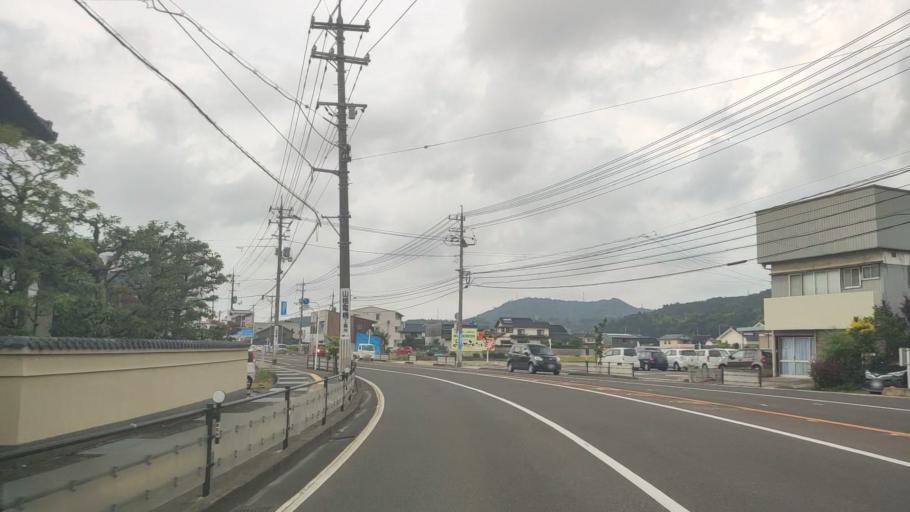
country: JP
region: Tottori
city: Kurayoshi
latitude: 35.4422
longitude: 133.8492
